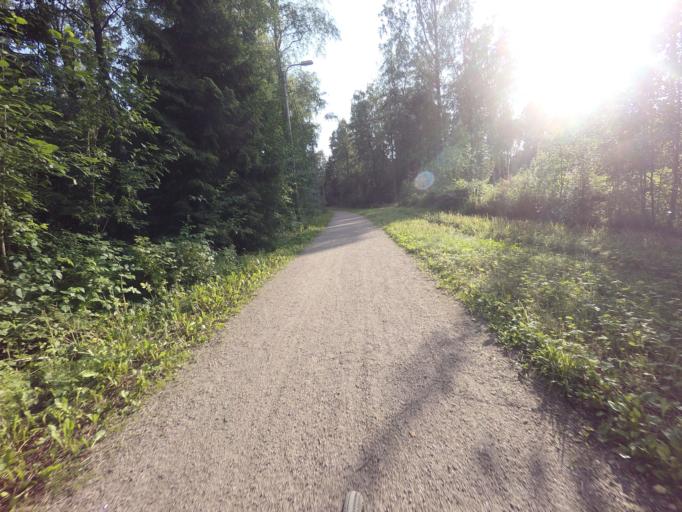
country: FI
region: Uusimaa
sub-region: Helsinki
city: Espoo
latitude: 60.1649
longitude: 24.6411
